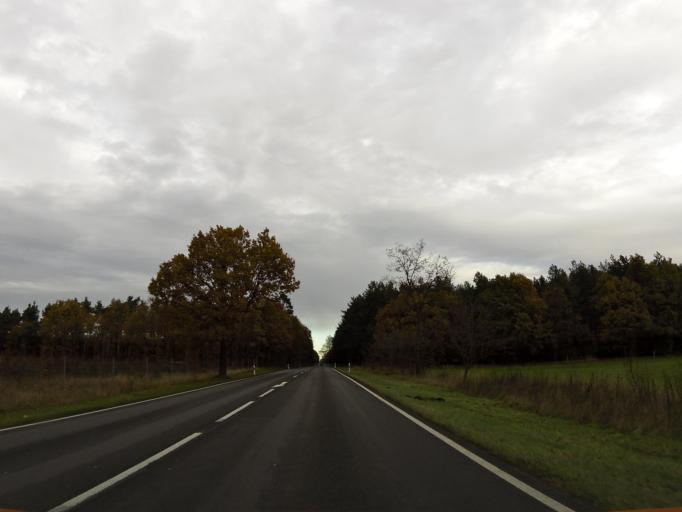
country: DE
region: Saxony-Anhalt
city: Letzlingen
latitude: 52.3803
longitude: 11.4658
